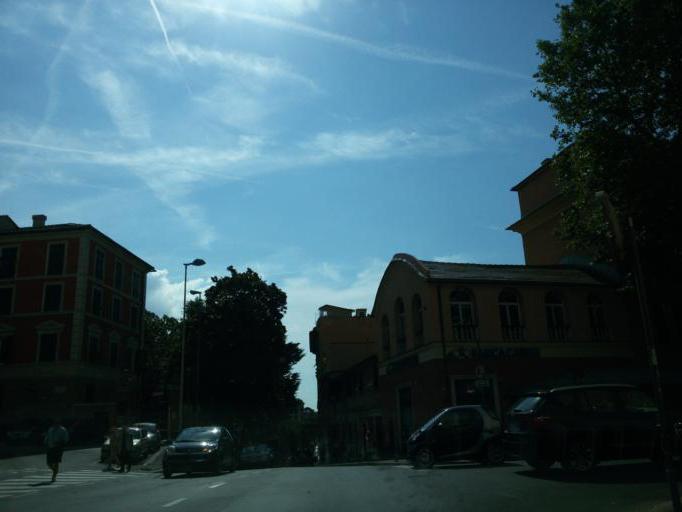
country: IT
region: Liguria
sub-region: Provincia di Genova
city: Genoa
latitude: 44.3997
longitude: 8.9607
